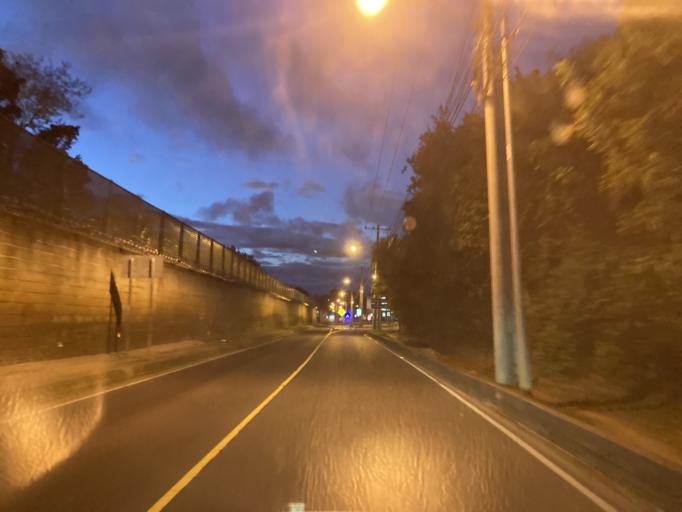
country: GT
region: Guatemala
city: Santa Catarina Pinula
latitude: 14.6043
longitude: -90.4680
